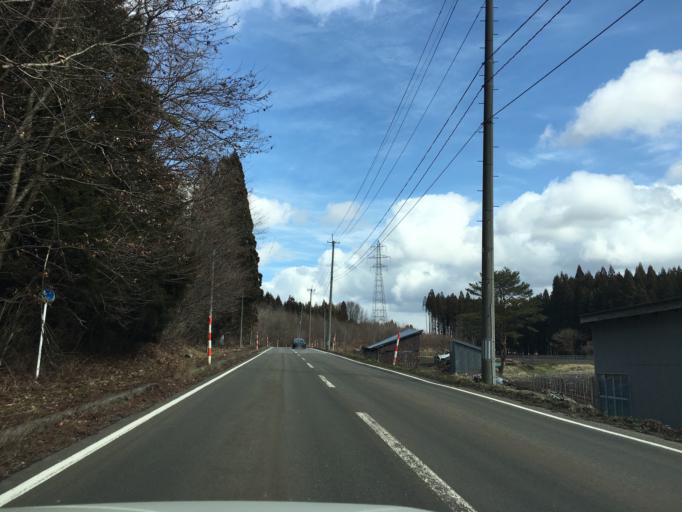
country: JP
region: Akita
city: Odate
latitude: 40.2015
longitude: 140.5404
